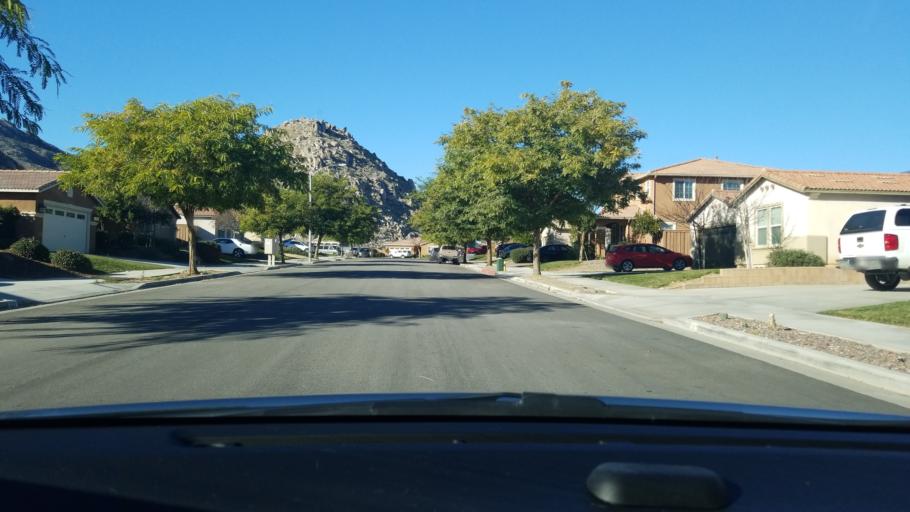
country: US
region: California
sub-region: Riverside County
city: Green Acres
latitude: 33.7977
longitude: -117.0366
